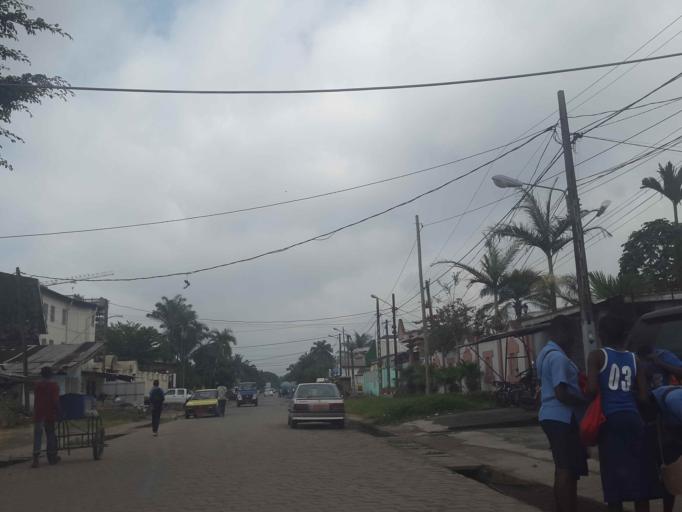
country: CM
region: Littoral
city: Douala
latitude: 4.0301
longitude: 9.7015
